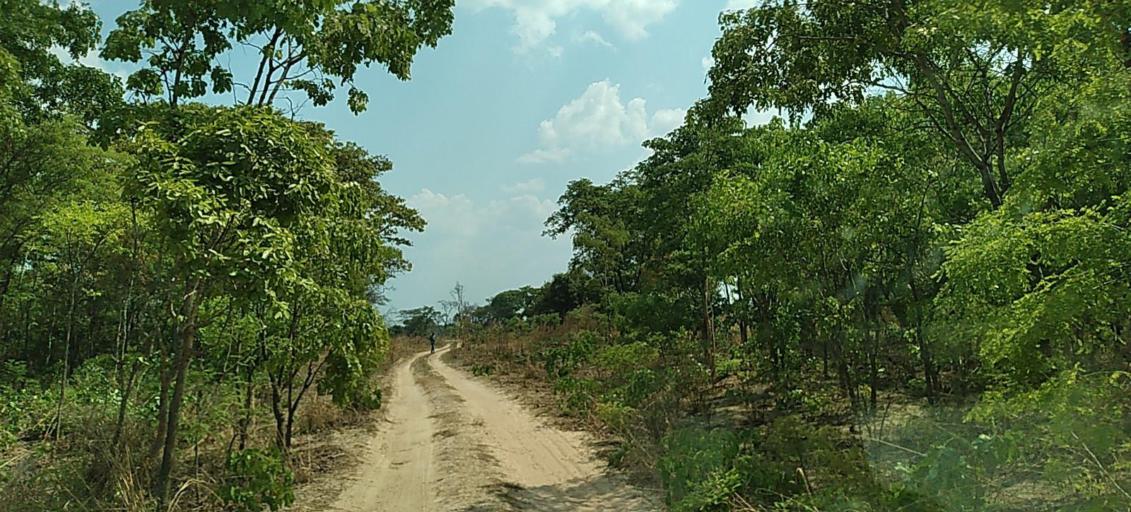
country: ZM
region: Copperbelt
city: Mpongwe
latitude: -13.8700
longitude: 27.9241
